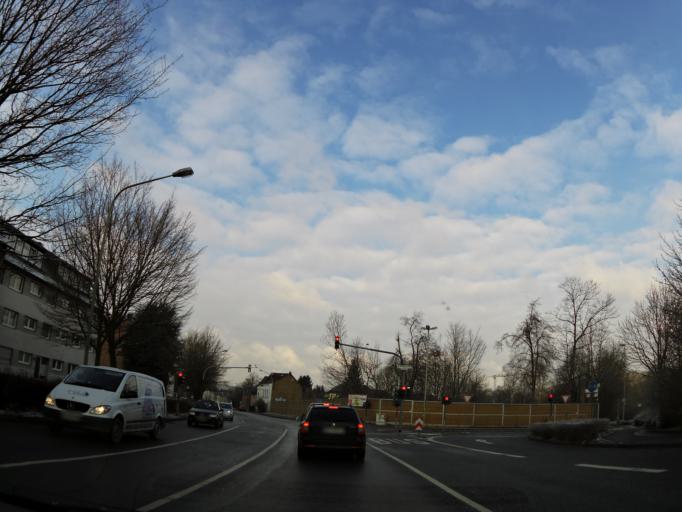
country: DE
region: North Rhine-Westphalia
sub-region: Regierungsbezirk Koln
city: Herzogenrath
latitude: 50.8632
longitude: 6.1033
